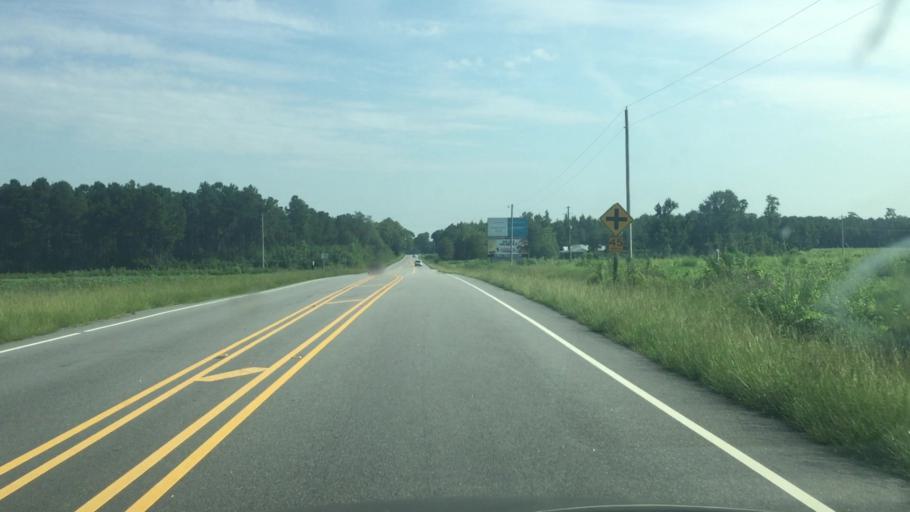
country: US
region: North Carolina
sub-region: Columbus County
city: Chadbourn
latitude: 34.2613
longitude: -78.8162
